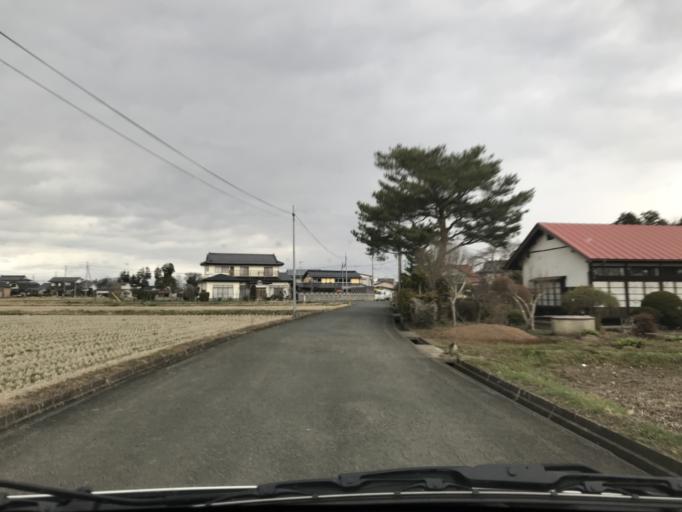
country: JP
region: Iwate
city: Mizusawa
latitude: 39.0855
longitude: 141.1737
